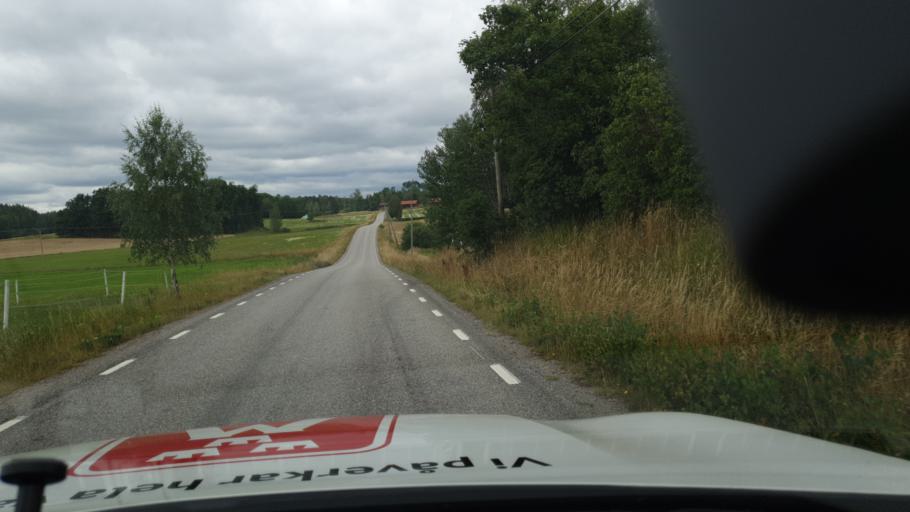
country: SE
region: Soedermanland
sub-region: Gnesta Kommun
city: Gnesta
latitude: 59.0422
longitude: 17.2655
